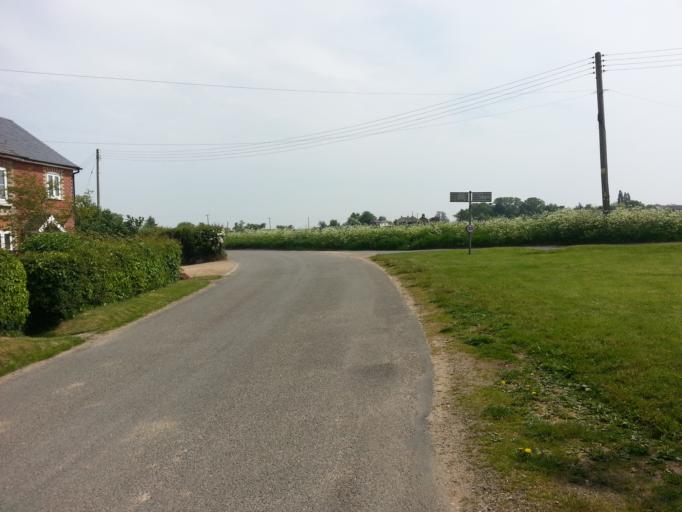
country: GB
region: England
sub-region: Suffolk
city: East Bergholt
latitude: 51.9962
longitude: 0.9893
